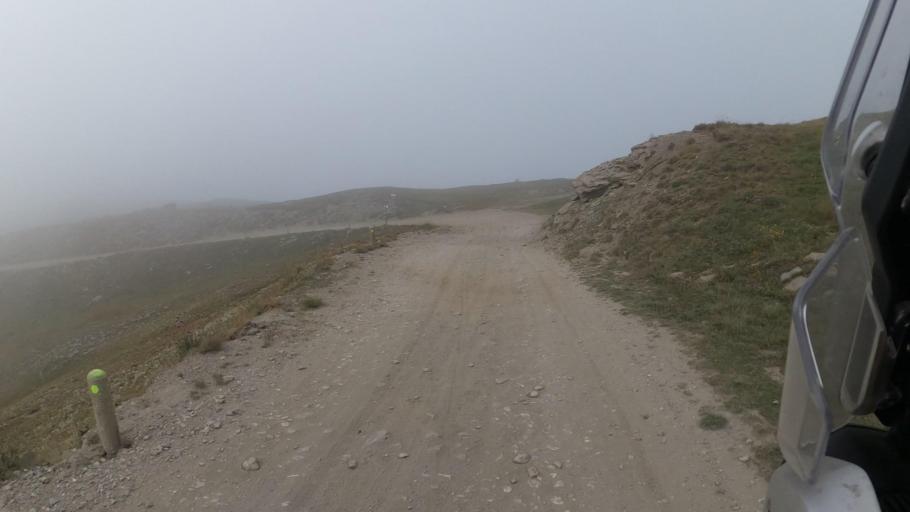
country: IT
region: Piedmont
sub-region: Provincia di Torino
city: Pragelato-Rua
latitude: 45.0556
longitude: 6.9356
